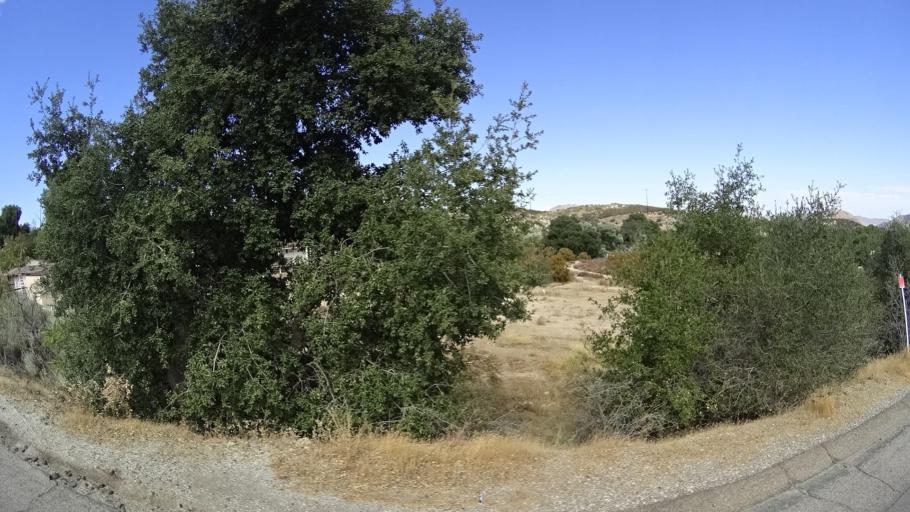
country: MX
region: Baja California
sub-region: Tecate
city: Cereso del Hongo
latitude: 32.6672
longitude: -116.2853
